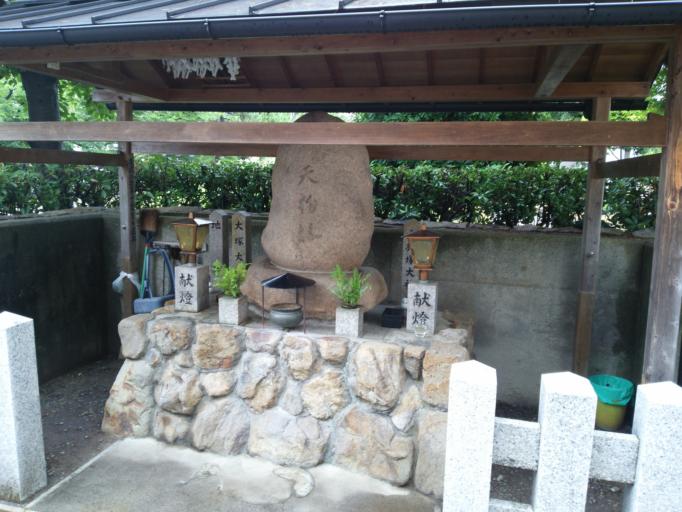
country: JP
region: Hyogo
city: Itami
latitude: 34.7639
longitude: 135.4253
